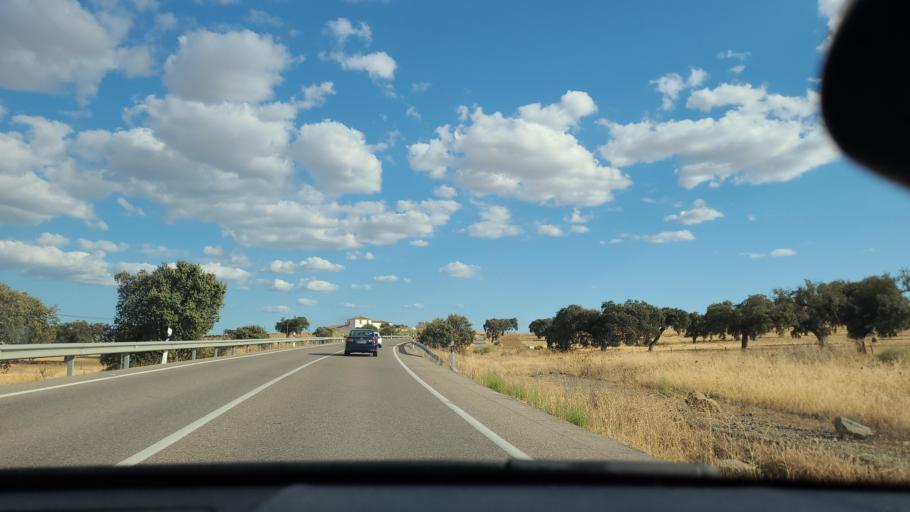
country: ES
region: Extremadura
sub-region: Provincia de Badajoz
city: Granja de Torrehermosa
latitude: 38.2847
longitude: -5.5204
